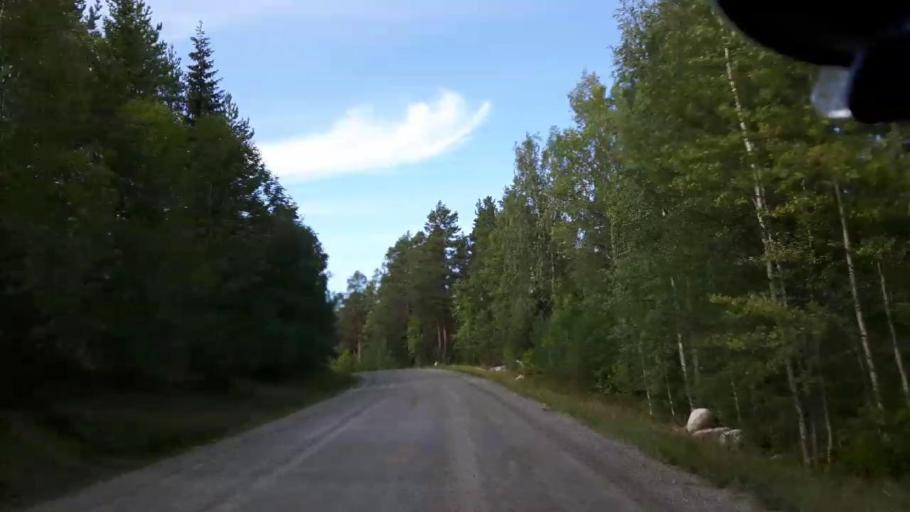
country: SE
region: Jaemtland
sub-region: Ragunda Kommun
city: Hammarstrand
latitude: 63.1481
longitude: 15.8888
